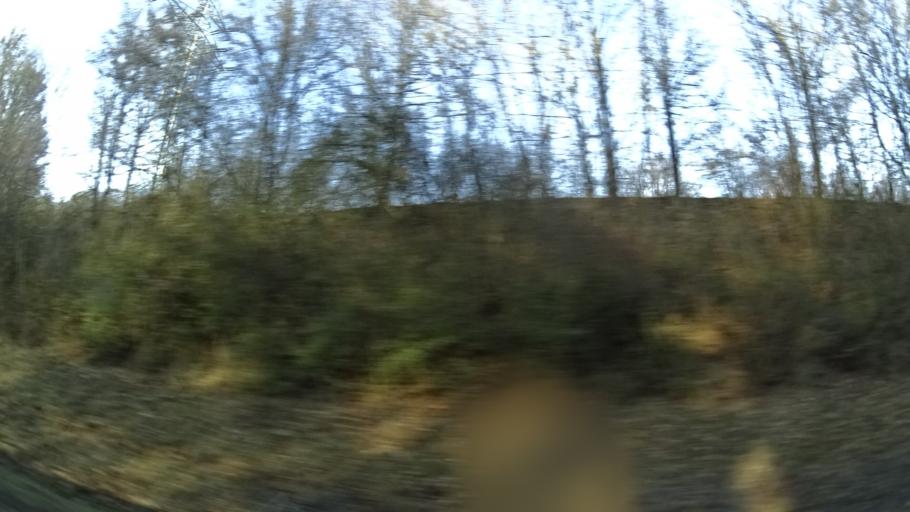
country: DE
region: Bavaria
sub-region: Regierungsbezirk Unterfranken
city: Zeitlofs
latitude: 50.3188
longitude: 9.6071
